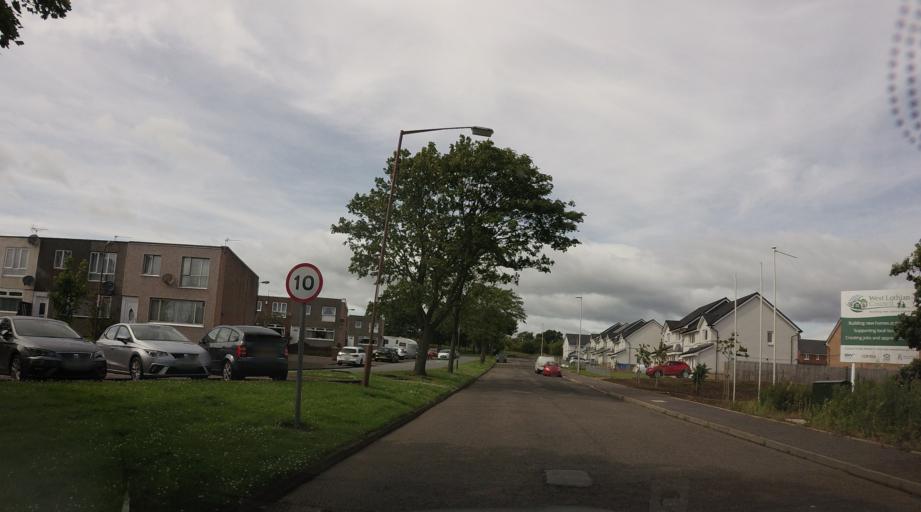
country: GB
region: Scotland
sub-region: West Lothian
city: Broxburn
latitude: 55.9358
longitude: -3.5013
